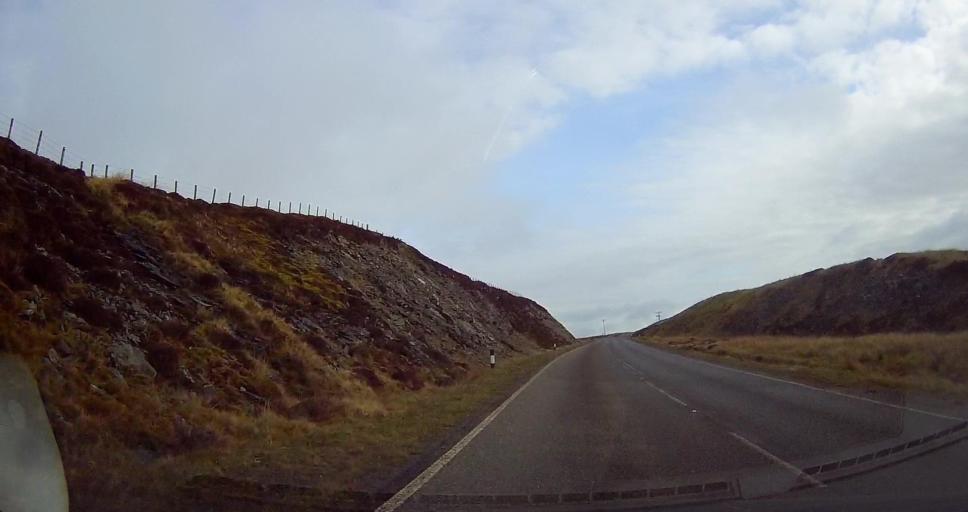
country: GB
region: Scotland
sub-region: Shetland Islands
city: Sandwick
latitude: 60.0740
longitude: -1.2309
